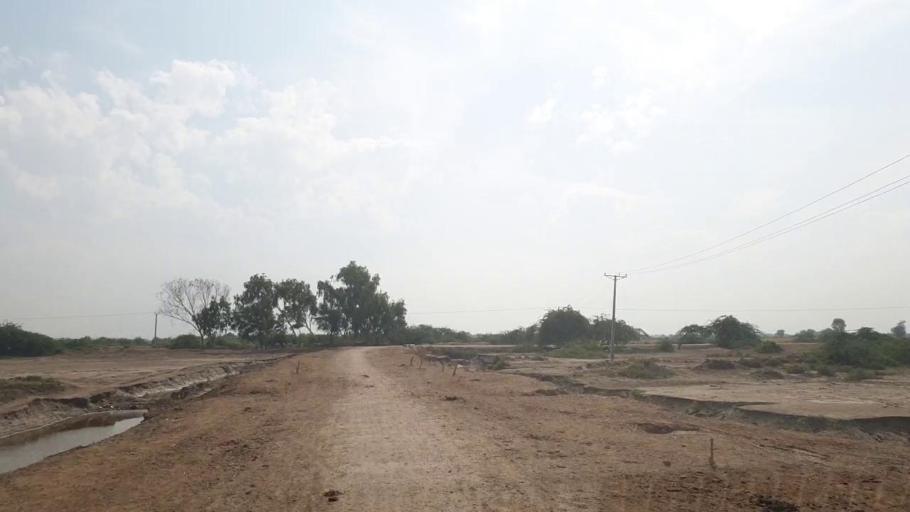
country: PK
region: Sindh
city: Rajo Khanani
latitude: 24.9701
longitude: 69.0194
